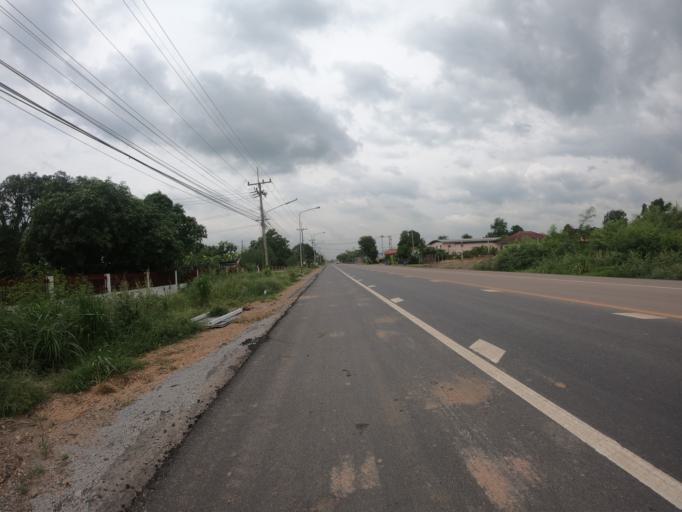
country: TH
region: Pathum Thani
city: Nong Suea
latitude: 14.0392
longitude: 100.8701
